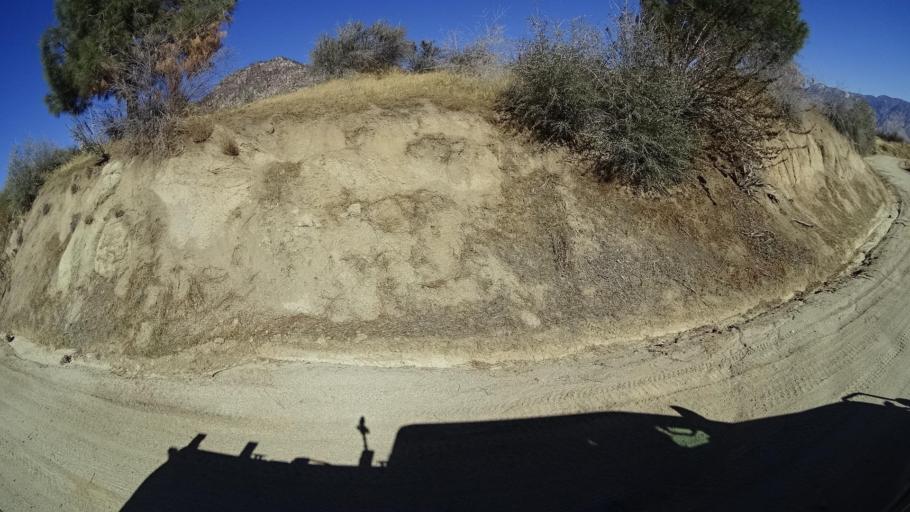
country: US
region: California
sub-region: Kern County
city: Alta Sierra
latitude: 35.7141
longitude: -118.5186
